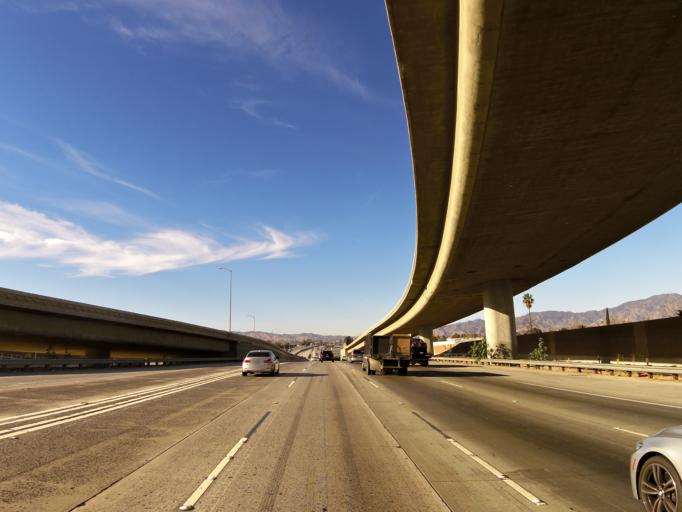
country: US
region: California
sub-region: Los Angeles County
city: San Fernando
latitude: 34.2335
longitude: -118.4100
